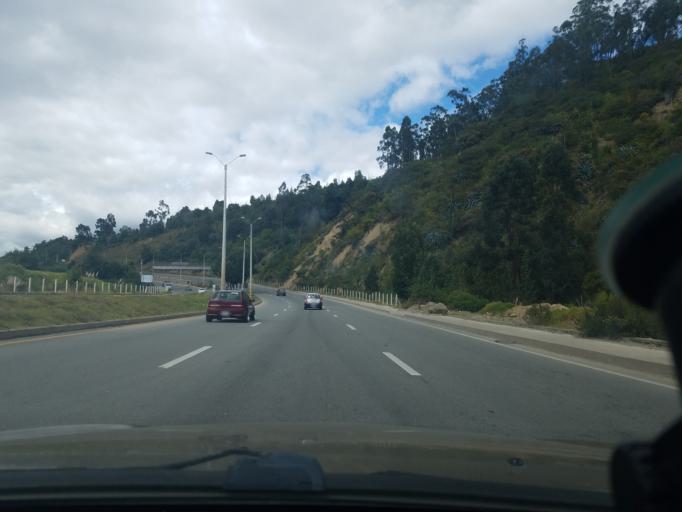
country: EC
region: Azuay
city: Llacao
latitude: -2.8637
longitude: -78.9309
